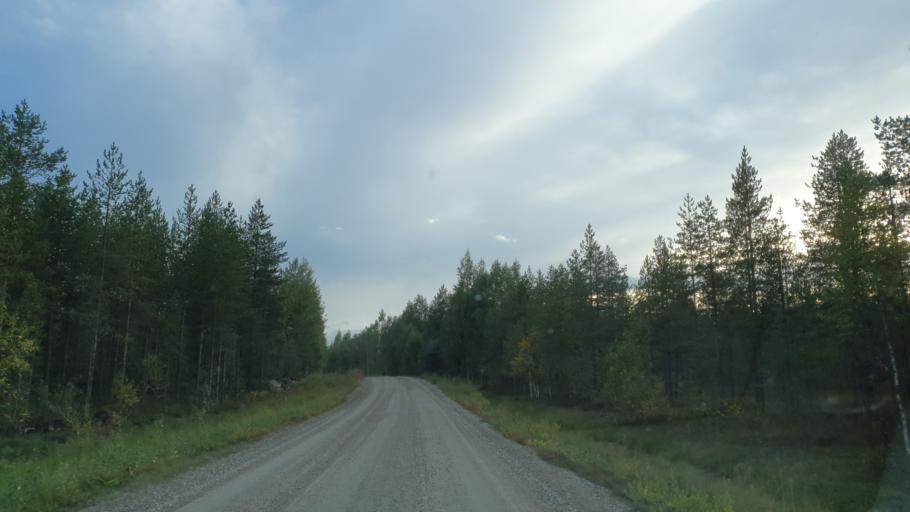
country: FI
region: Kainuu
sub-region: Kehys-Kainuu
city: Kuhmo
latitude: 64.3811
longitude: 29.5519
